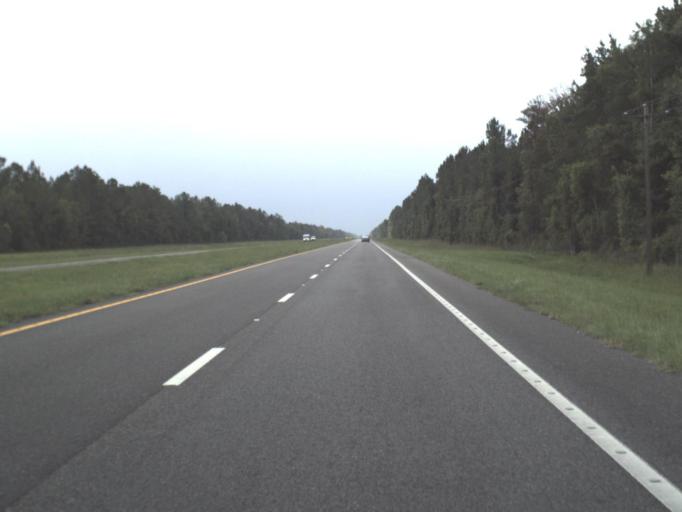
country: US
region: Florida
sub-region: Levy County
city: Chiefland
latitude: 29.3755
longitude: -82.7981
